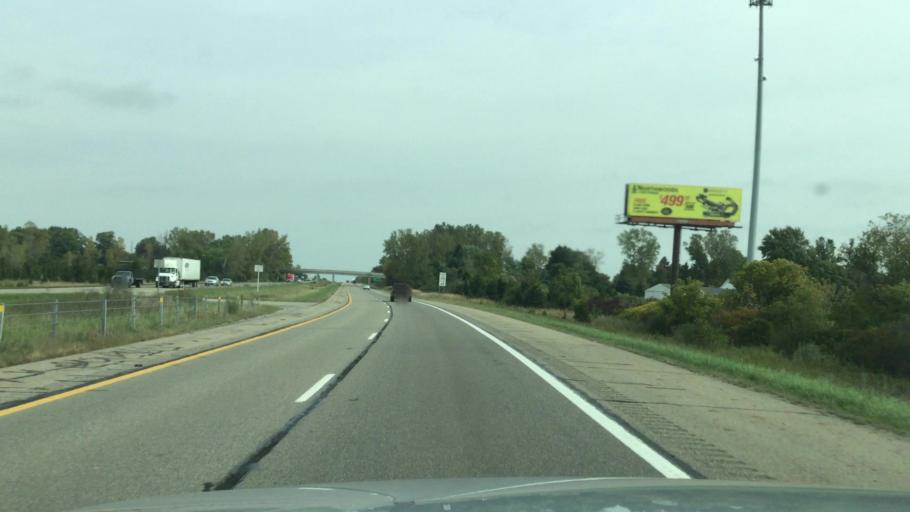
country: US
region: Michigan
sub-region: Shiawassee County
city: Durand
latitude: 42.9310
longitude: -83.9917
